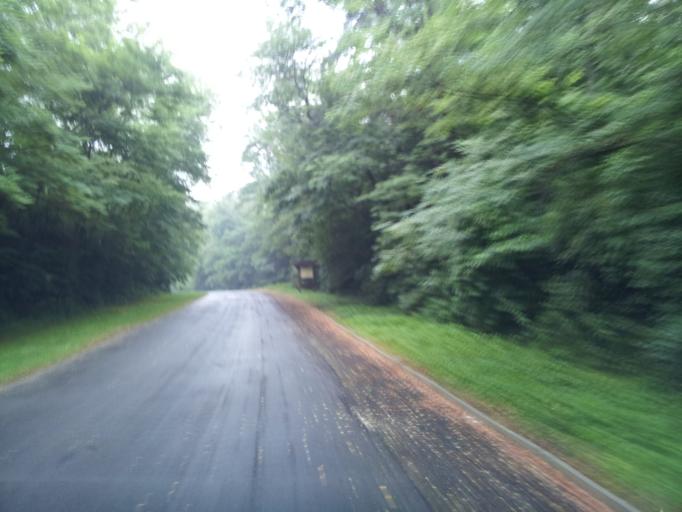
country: HU
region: Zala
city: Zalalovo
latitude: 46.8732
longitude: 16.5511
